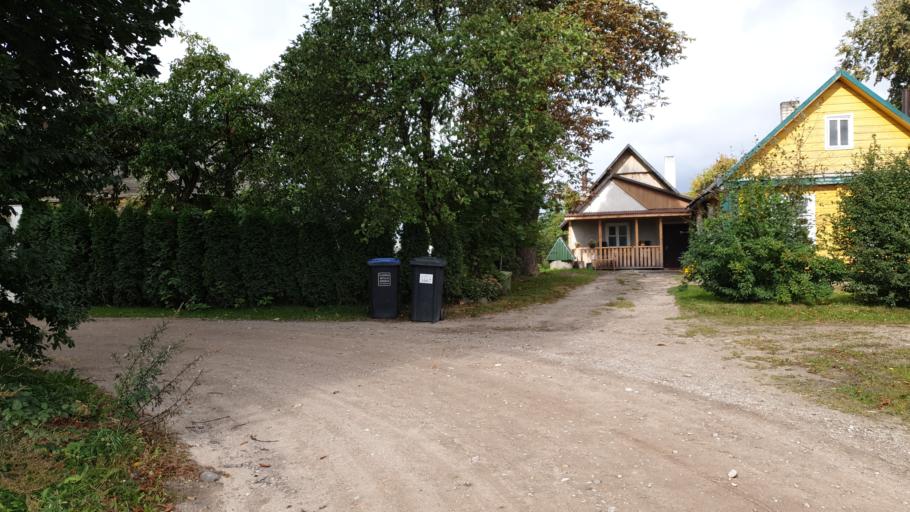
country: LT
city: Moletai
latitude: 55.2344
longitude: 25.4178
